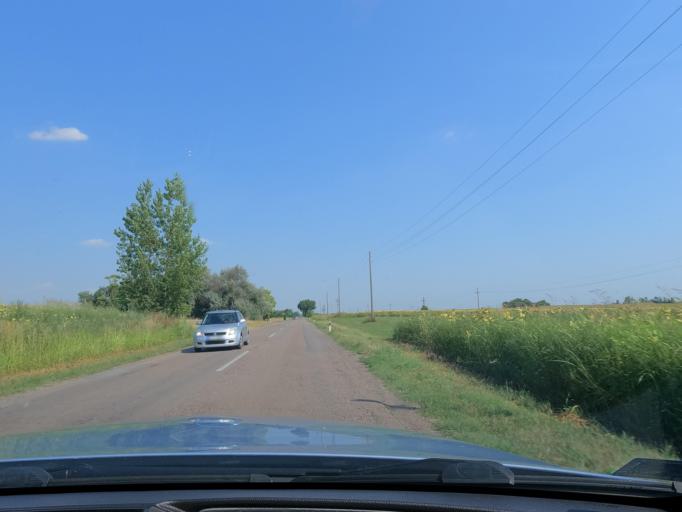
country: RS
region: Autonomna Pokrajina Vojvodina
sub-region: Severnobacki Okrug
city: Mali Igos
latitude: 45.7535
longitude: 19.7822
